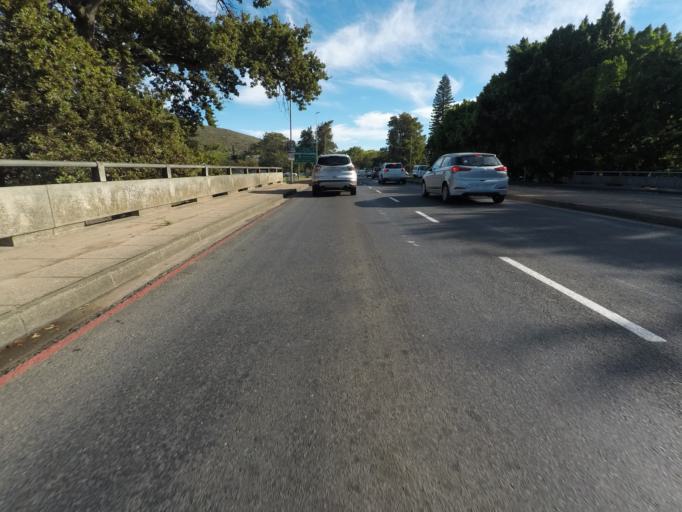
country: ZA
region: Western Cape
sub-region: Cape Winelands District Municipality
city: Stellenbosch
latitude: -33.9416
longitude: 18.8520
